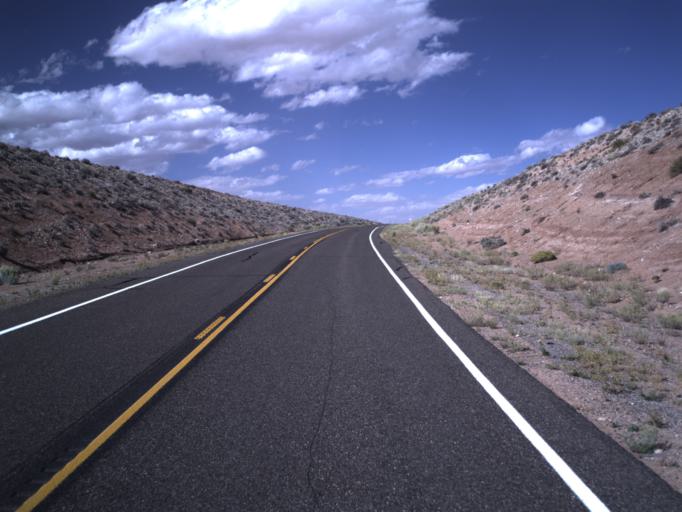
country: US
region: Utah
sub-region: Wayne County
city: Loa
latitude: 38.1133
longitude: -110.6243
